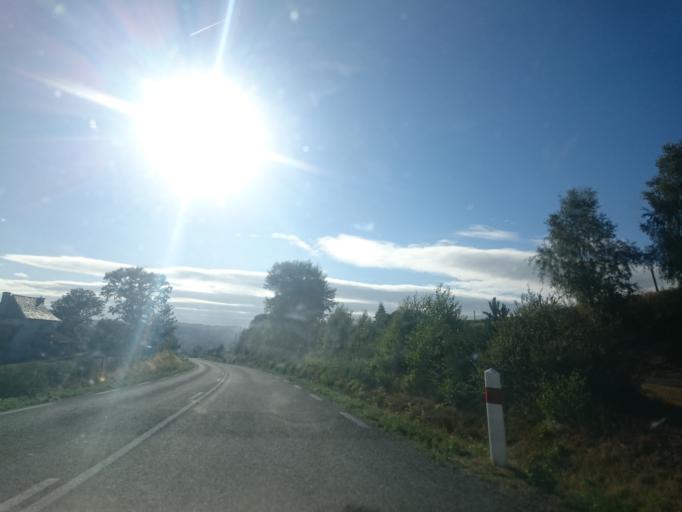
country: FR
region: Midi-Pyrenees
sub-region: Departement de l'Aveyron
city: Entraygues-sur-Truyere
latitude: 44.7432
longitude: 2.5000
